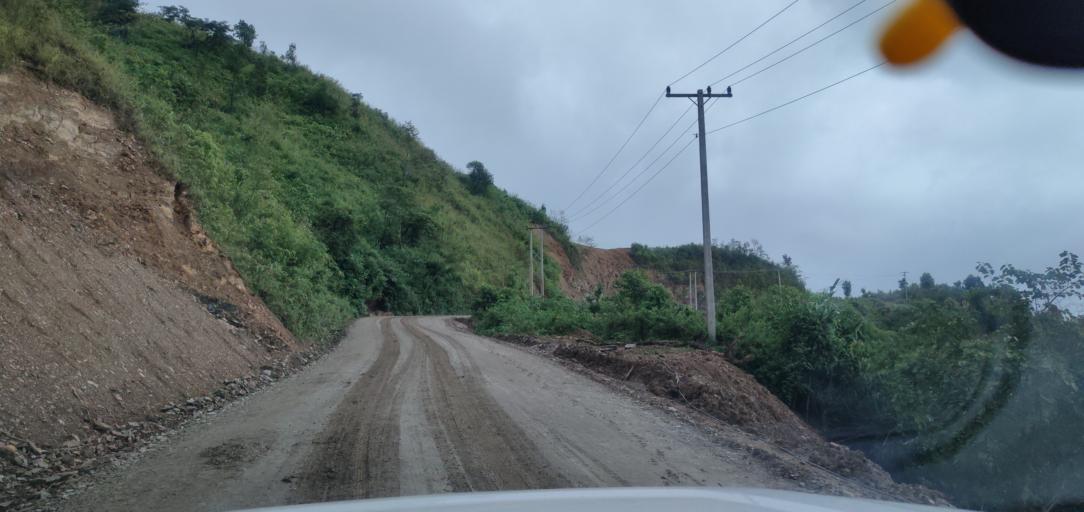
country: LA
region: Phongsali
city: Phongsali
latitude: 21.4248
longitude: 102.1708
